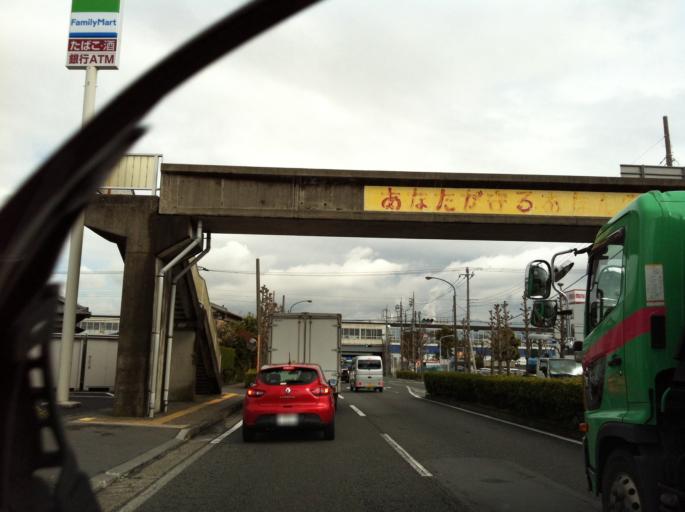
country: JP
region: Shizuoka
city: Fuji
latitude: 35.1405
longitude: 138.6624
